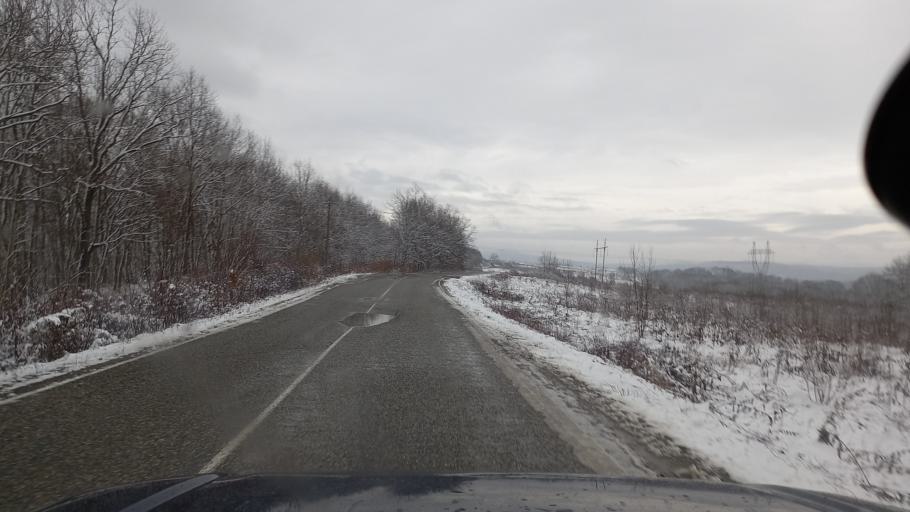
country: RU
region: Adygeya
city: Abadzekhskaya
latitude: 44.3484
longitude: 40.3614
